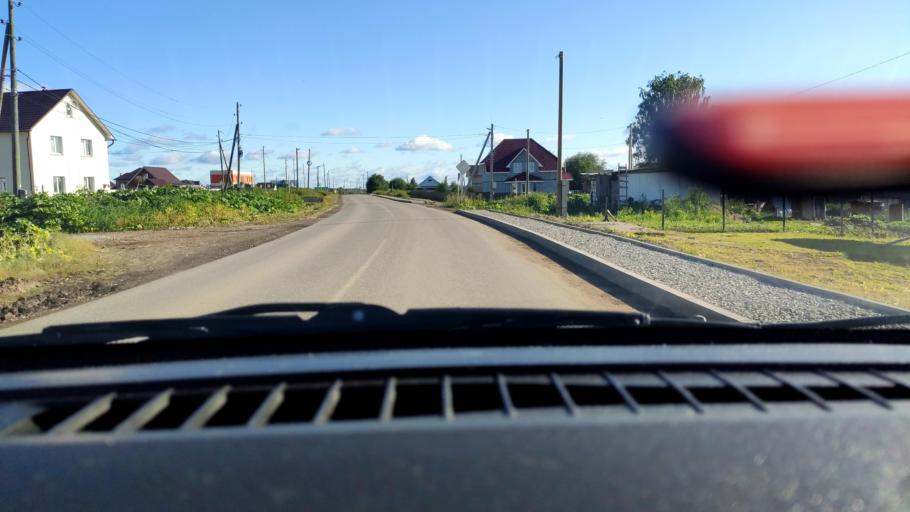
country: RU
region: Perm
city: Kultayevo
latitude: 57.8641
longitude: 55.9152
